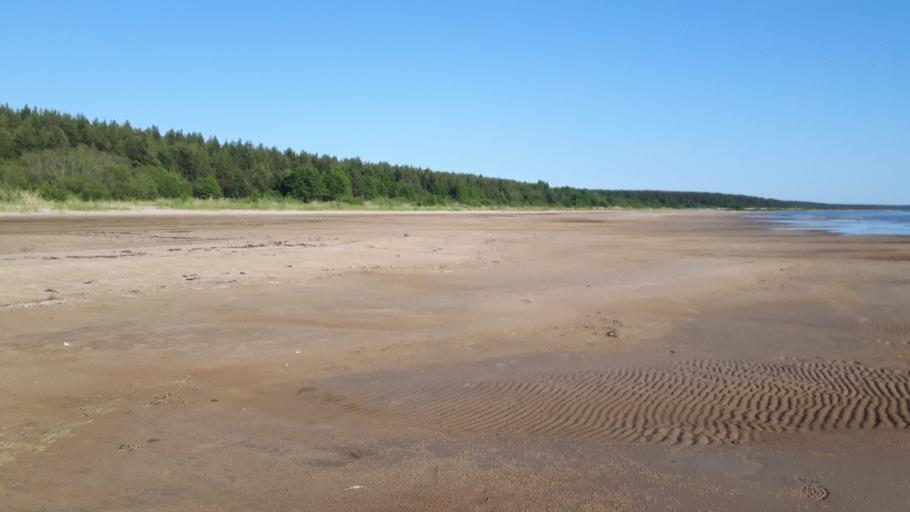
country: LV
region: Salacgrivas
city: Salacgriva
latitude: 57.6924
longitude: 24.3523
